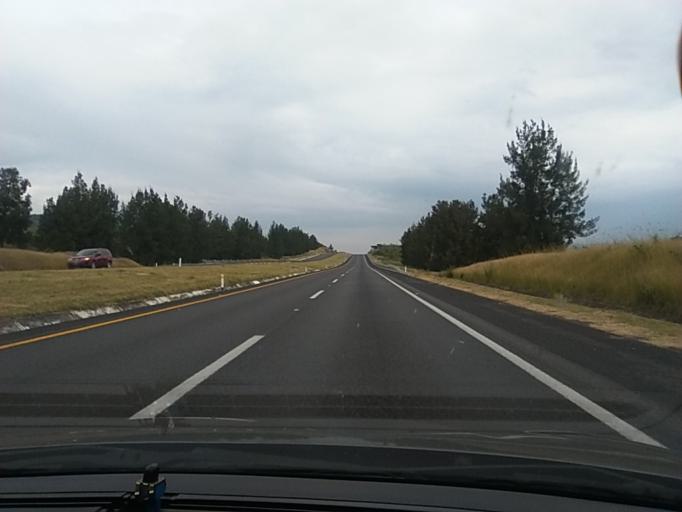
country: MX
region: Michoacan
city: Churintzio
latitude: 20.1155
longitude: -102.0470
